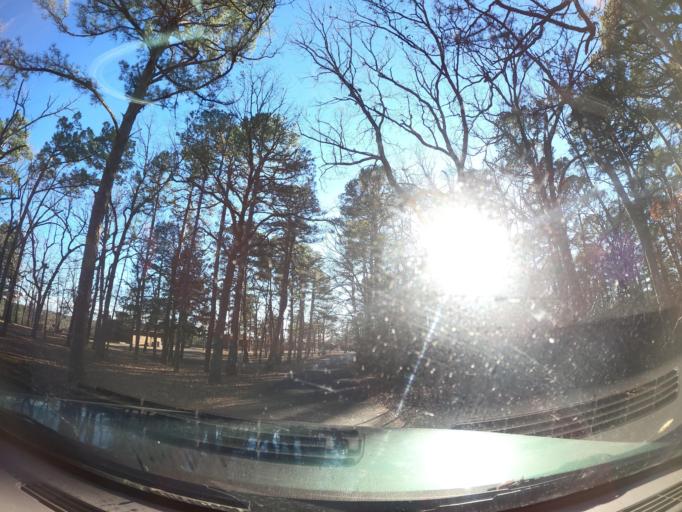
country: US
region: Oklahoma
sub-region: Latimer County
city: Wilburton
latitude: 34.9794
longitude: -95.3522
